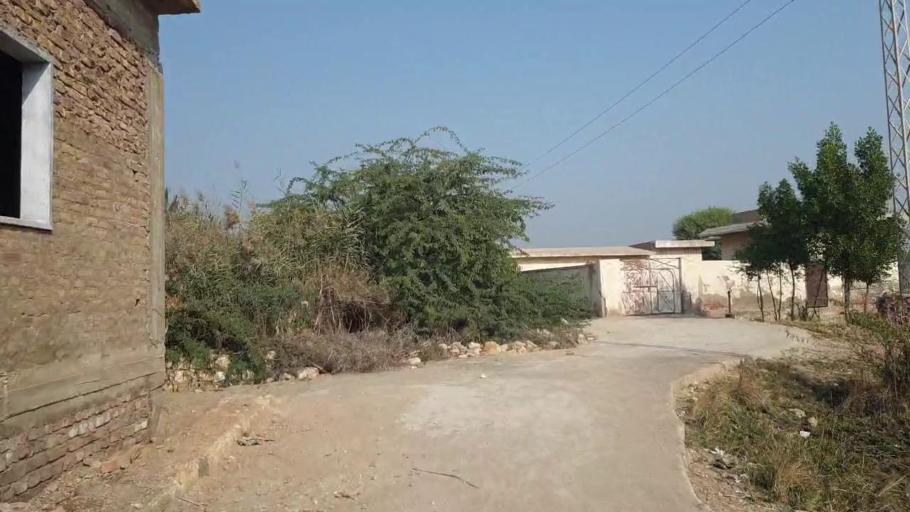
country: PK
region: Sindh
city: Kotri
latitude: 25.3315
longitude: 68.3239
